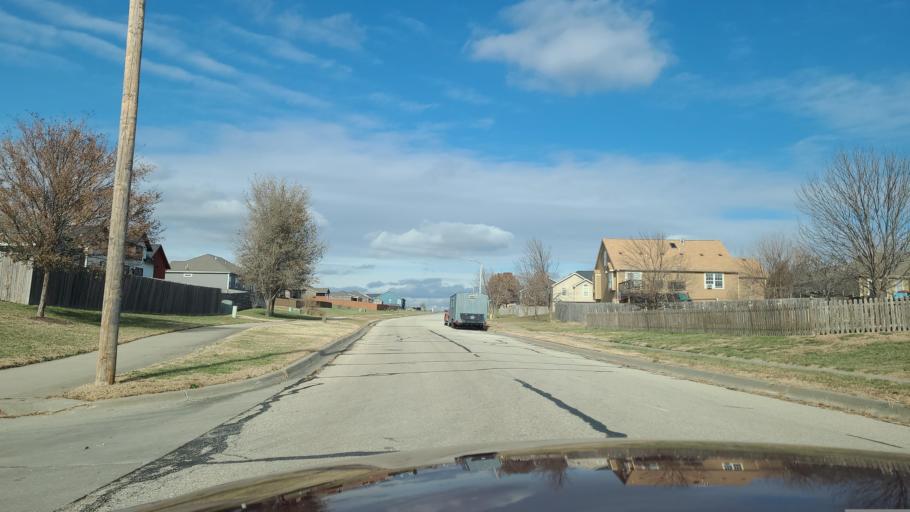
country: US
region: Kansas
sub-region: Douglas County
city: Eudora
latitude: 38.9146
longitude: -95.1012
